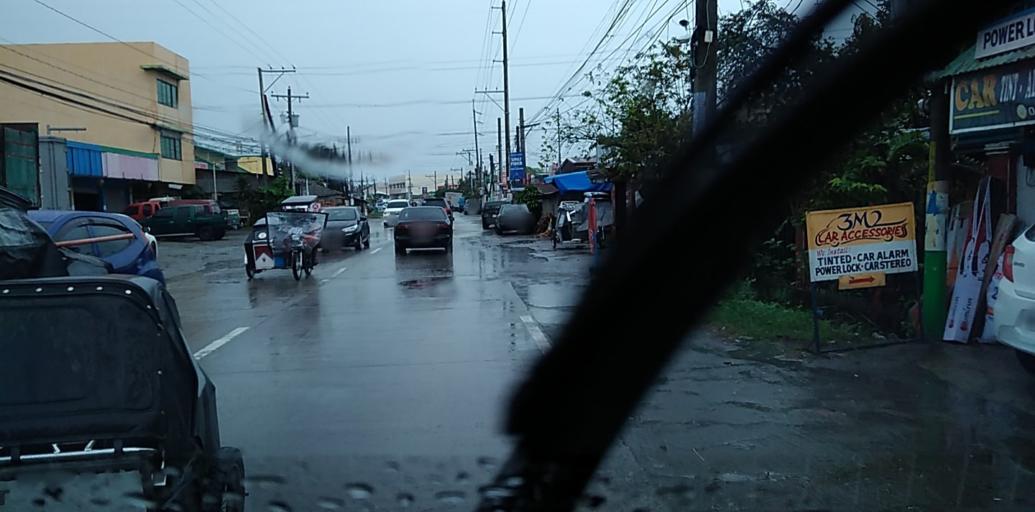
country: PH
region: Central Luzon
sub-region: Province of Pampanga
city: Mexico
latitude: 15.0562
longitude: 120.7152
